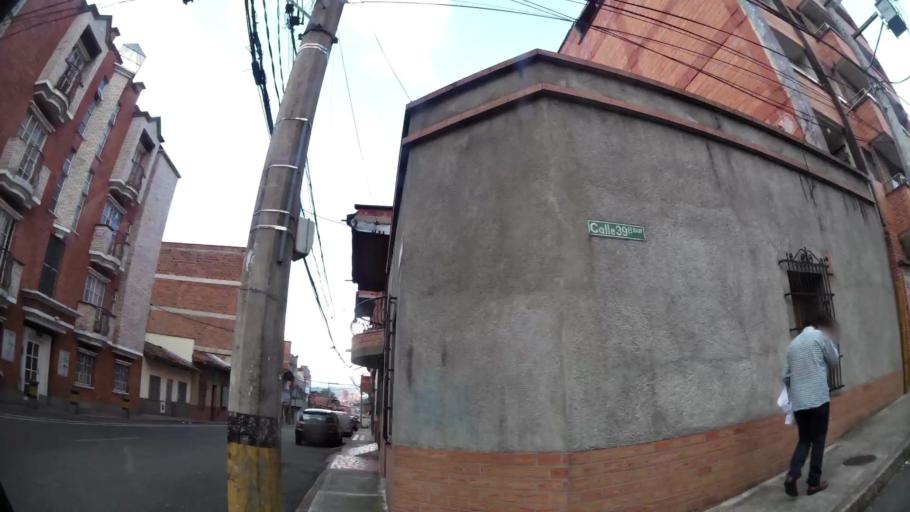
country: CO
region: Antioquia
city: Envigado
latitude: 6.1641
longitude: -75.5835
